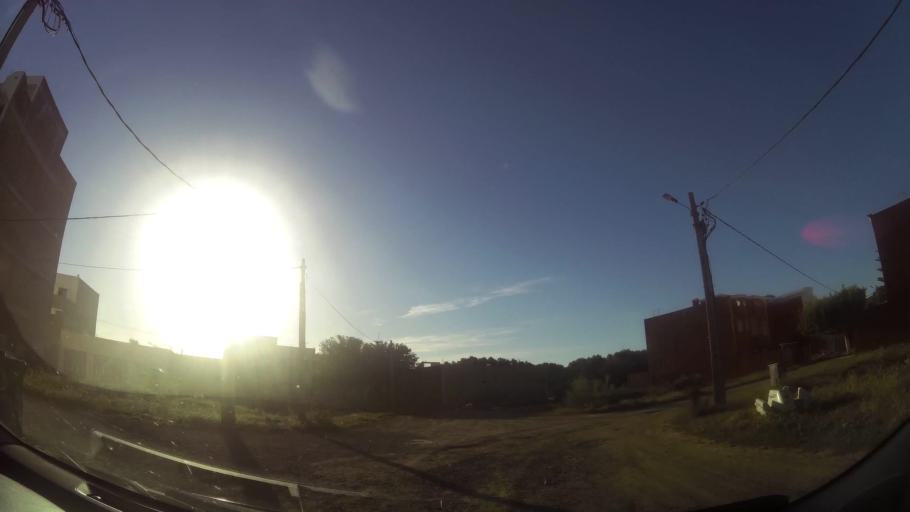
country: MA
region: Oriental
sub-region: Berkane-Taourirt
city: Madagh
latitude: 35.0881
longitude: -2.2481
